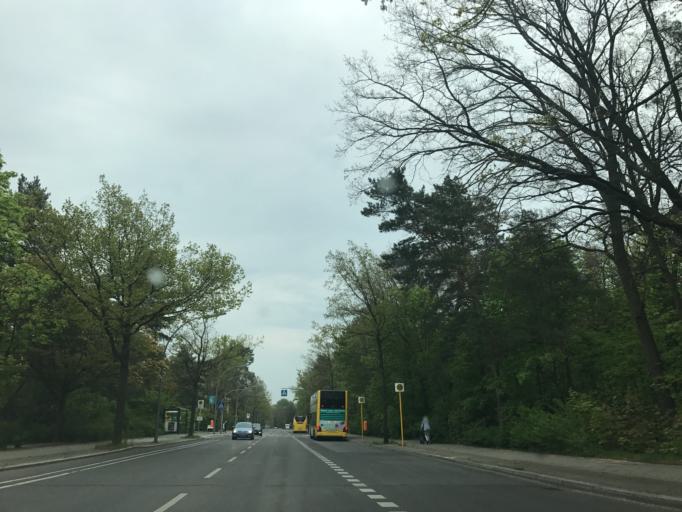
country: DE
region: Berlin
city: Falkenhagener Feld
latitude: 52.5614
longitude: 13.1579
